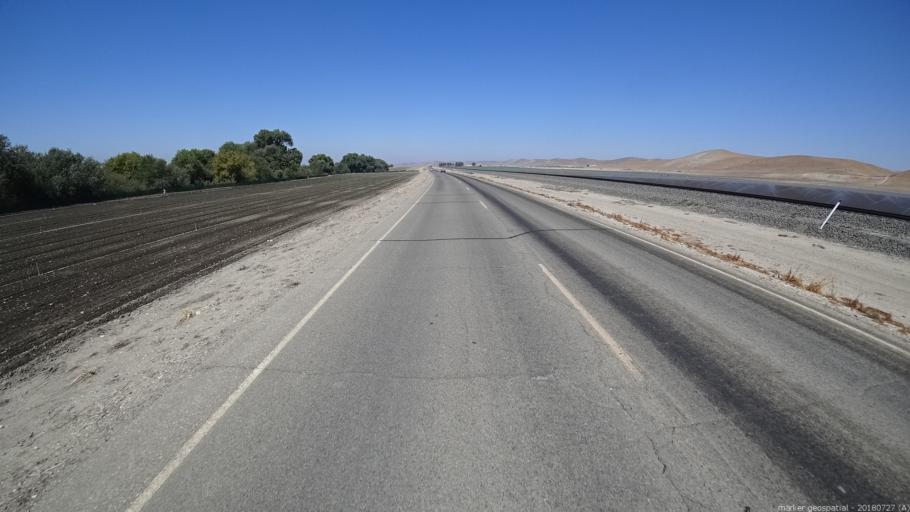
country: US
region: California
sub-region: Monterey County
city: King City
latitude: 36.0591
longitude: -120.9251
